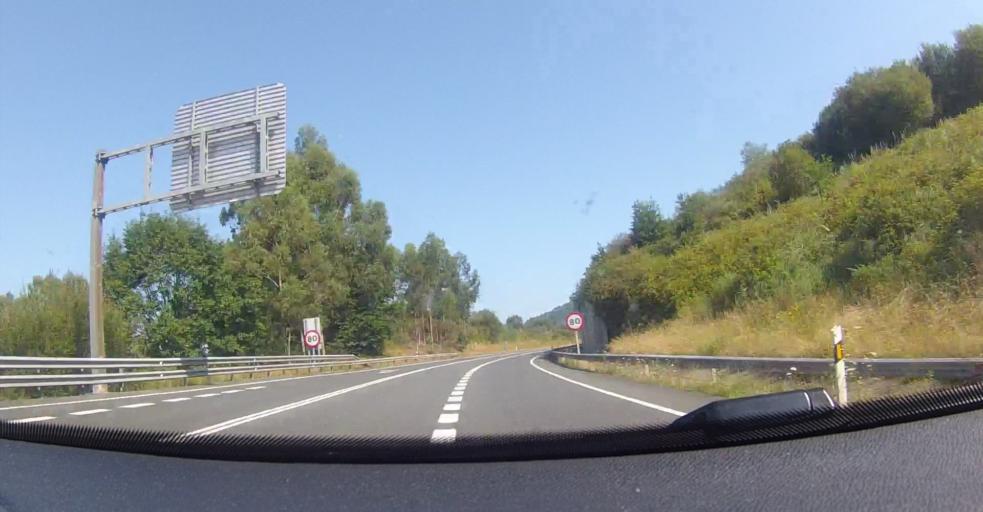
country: ES
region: Cantabria
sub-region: Provincia de Cantabria
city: Ampuero
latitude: 43.3509
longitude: -3.4138
